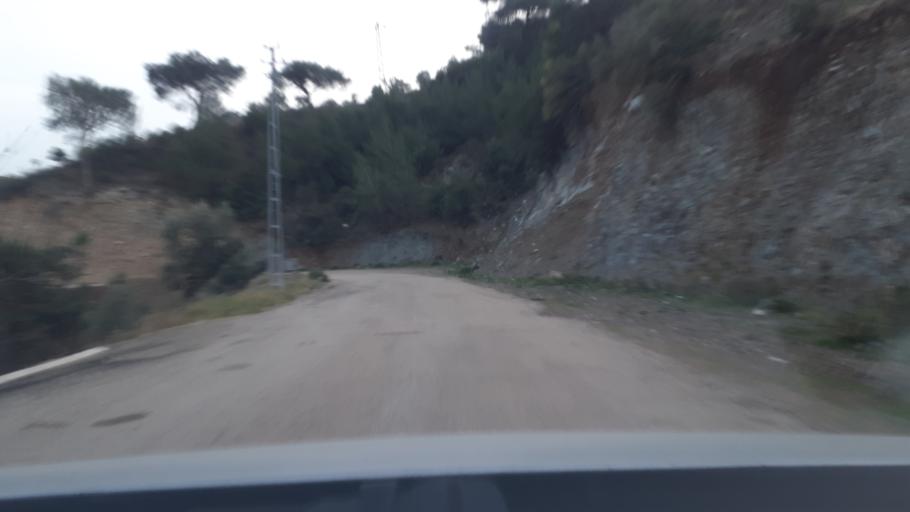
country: TR
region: Hatay
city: Kirikhan
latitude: 36.5324
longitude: 36.3149
